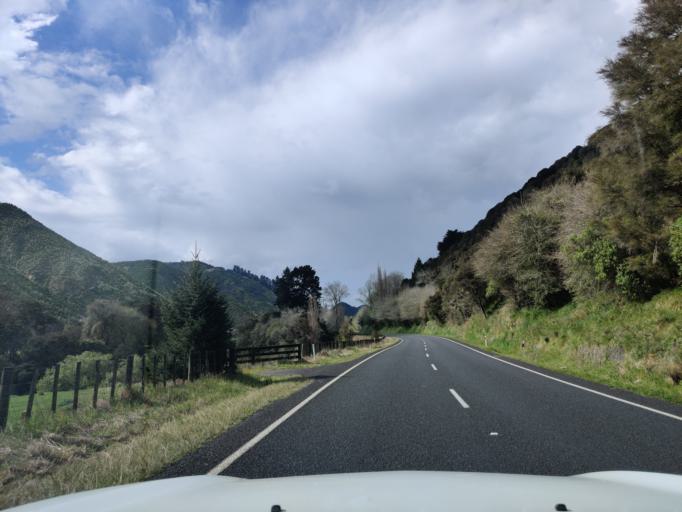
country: NZ
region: Manawatu-Wanganui
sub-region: Wanganui District
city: Wanganui
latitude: -39.8262
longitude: 175.1703
